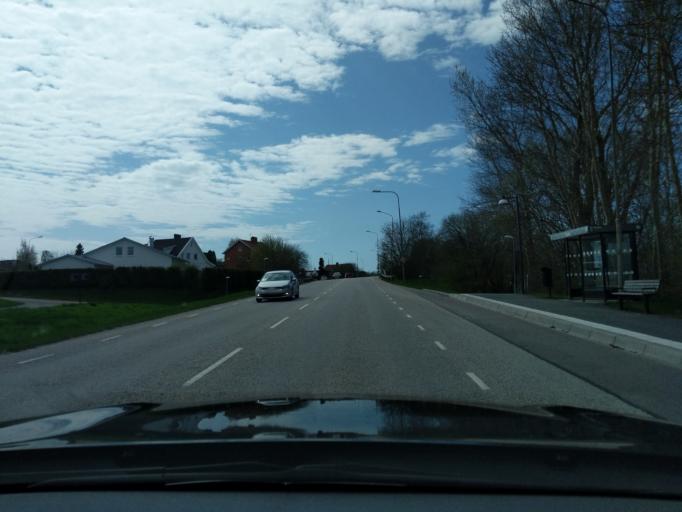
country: SE
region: Vaestra Goetaland
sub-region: Goteborg
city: Majorna
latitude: 57.6370
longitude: 11.9442
